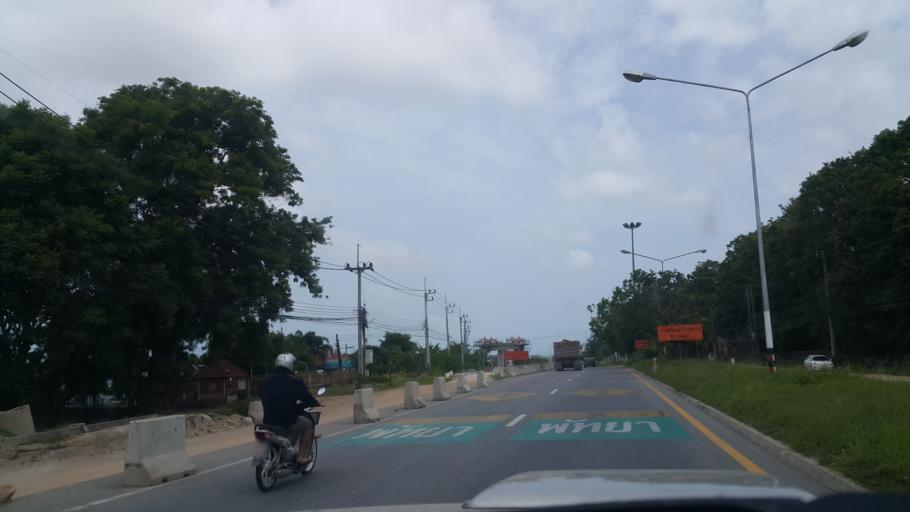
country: TH
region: Rayong
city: Ban Chang
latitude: 12.7150
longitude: 101.0354
